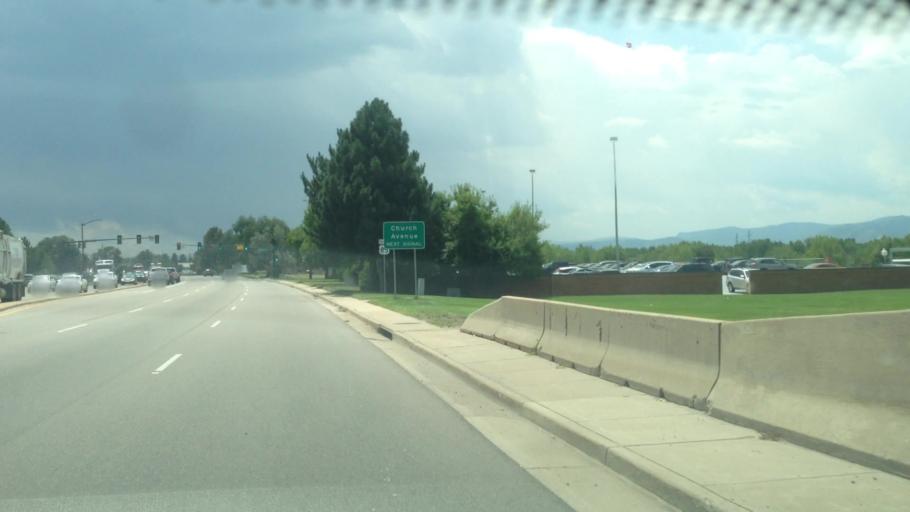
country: US
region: Colorado
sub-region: Arapahoe County
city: Littleton
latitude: 39.6118
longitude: -105.0213
